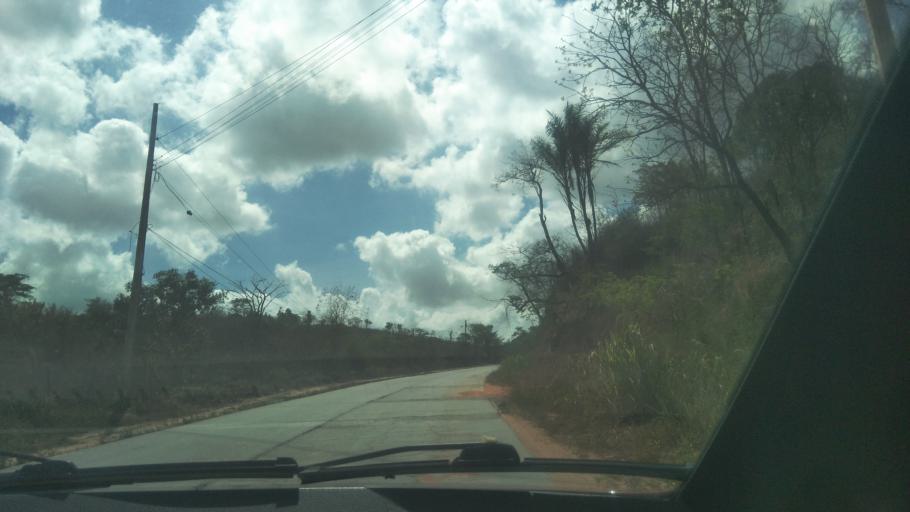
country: BR
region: Pernambuco
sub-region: Vitoria De Santo Antao
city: Vitoria de Santo Antao
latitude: -8.1348
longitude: -35.2779
